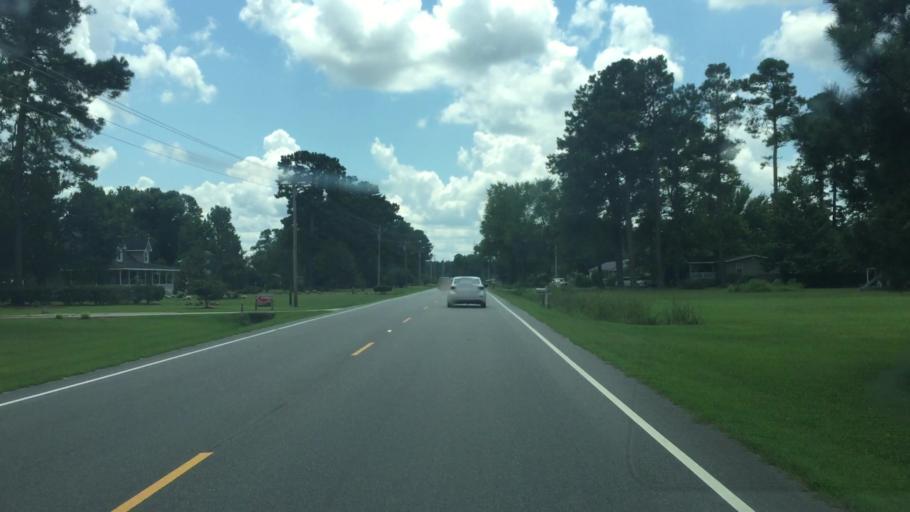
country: US
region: North Carolina
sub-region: Columbus County
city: Chadbourn
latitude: 34.2399
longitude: -78.8223
